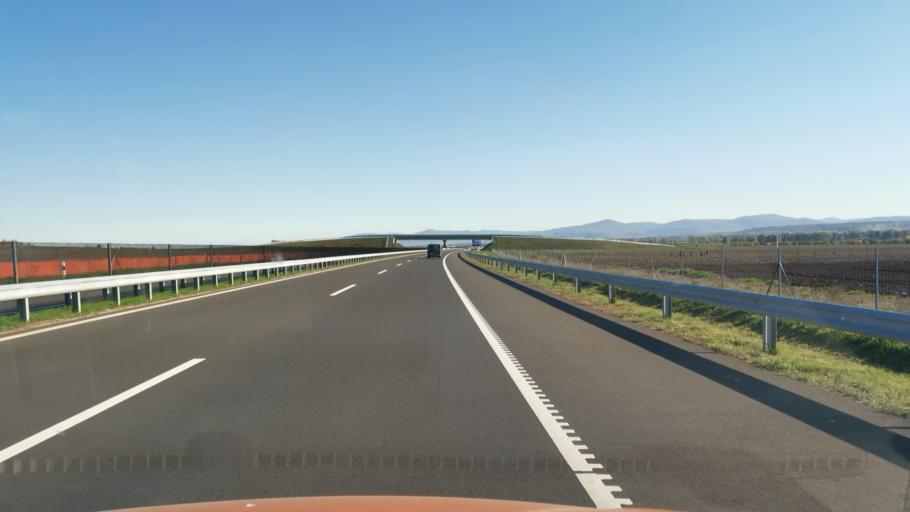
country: HU
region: Borsod-Abauj-Zemplen
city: Halmaj
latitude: 48.2863
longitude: 21.0175
